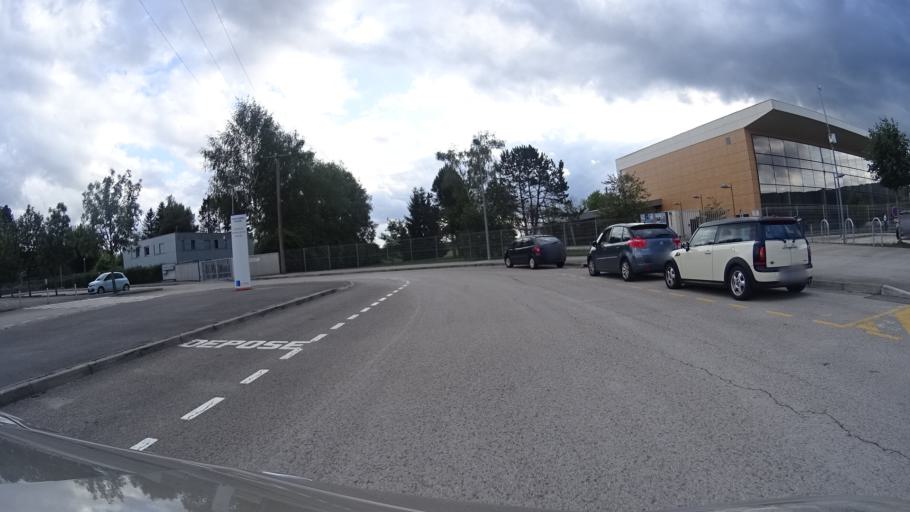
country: FR
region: Franche-Comte
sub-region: Departement du Doubs
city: Saone
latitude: 47.2271
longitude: 6.1137
